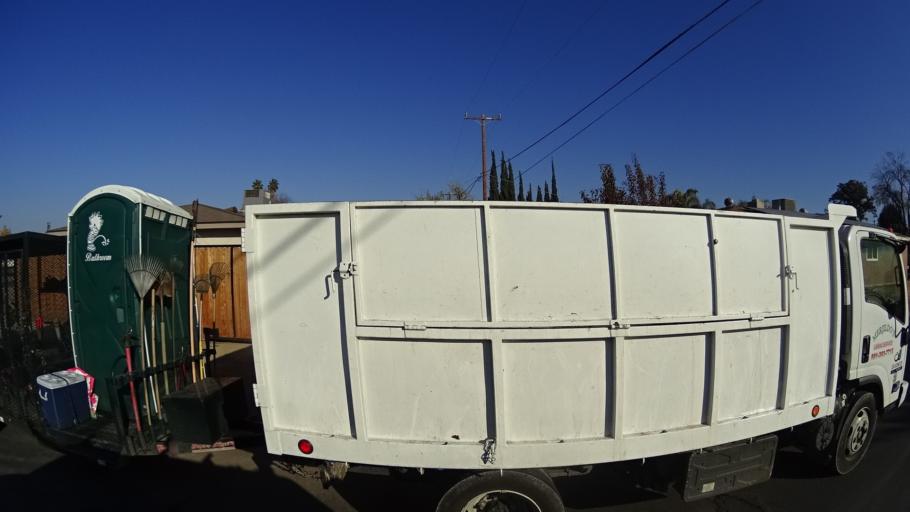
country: US
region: California
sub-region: Kern County
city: Greenfield
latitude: 35.3007
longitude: -119.0173
